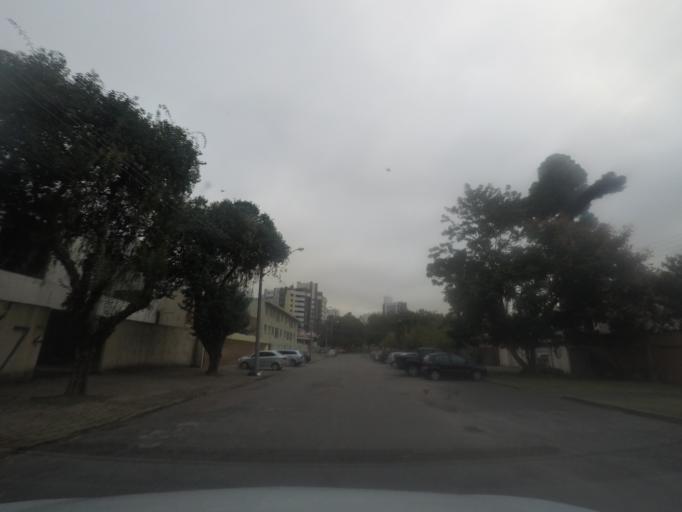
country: BR
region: Parana
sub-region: Curitiba
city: Curitiba
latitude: -25.4303
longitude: -49.2521
